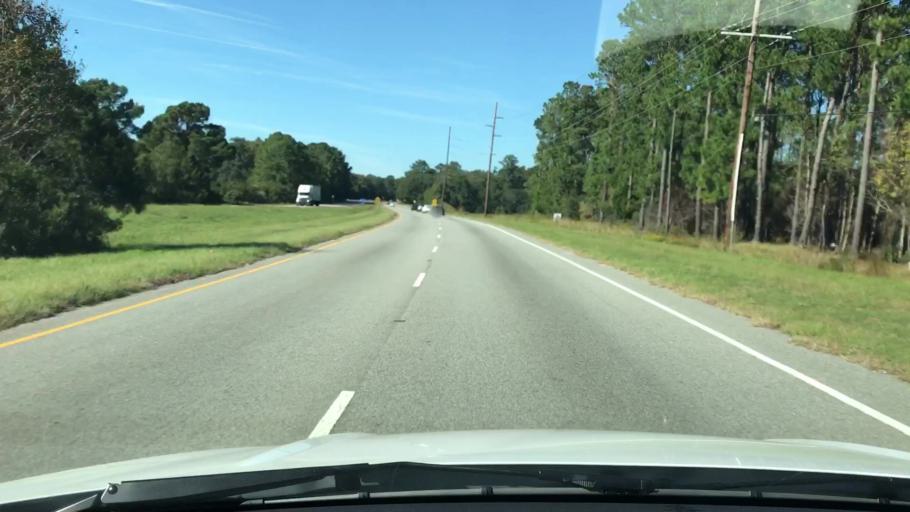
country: US
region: South Carolina
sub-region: Beaufort County
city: Laurel Bay
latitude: 32.5087
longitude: -80.7470
